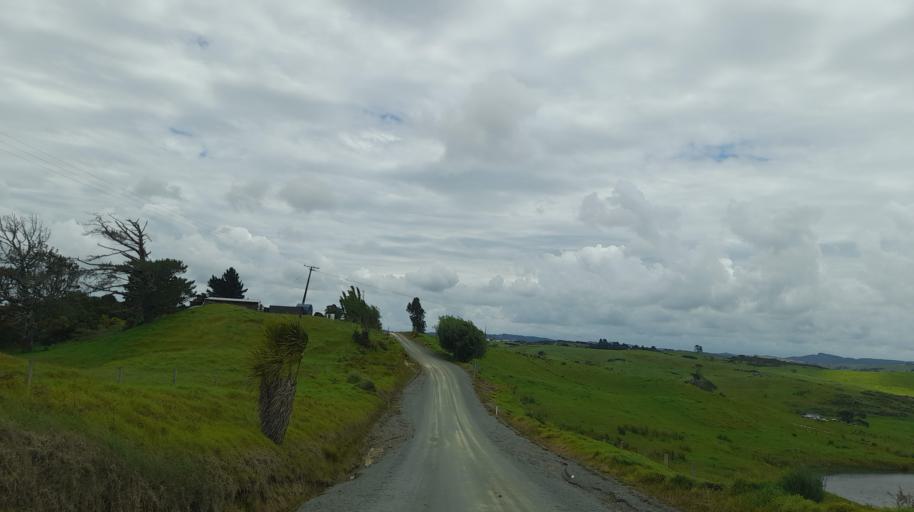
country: NZ
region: Auckland
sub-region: Auckland
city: Wellsford
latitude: -36.2659
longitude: 174.4099
